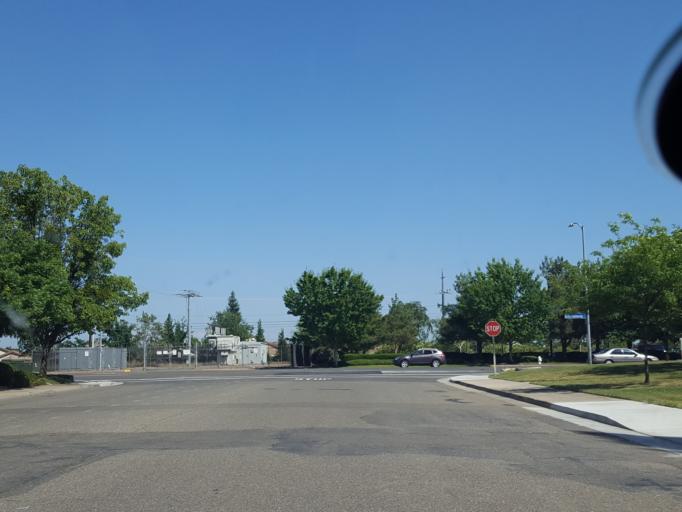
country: US
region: California
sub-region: Sacramento County
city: Rancho Cordova
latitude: 38.5783
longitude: -121.2908
